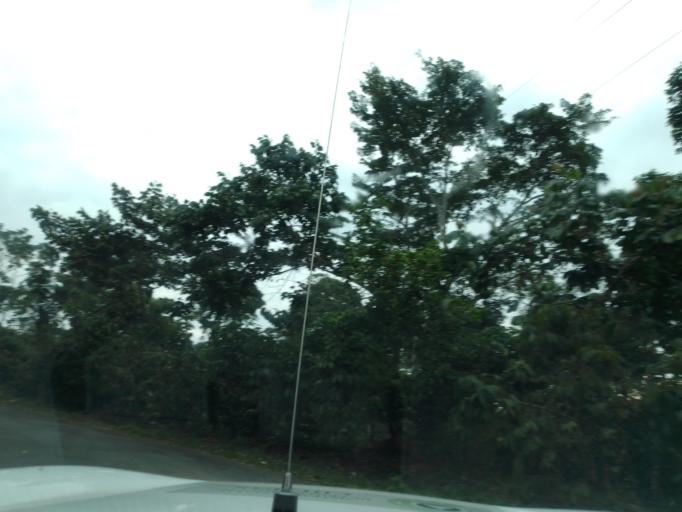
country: MX
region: Chiapas
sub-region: Union Juarez
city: Santo Domingo
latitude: 15.0495
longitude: -92.1207
